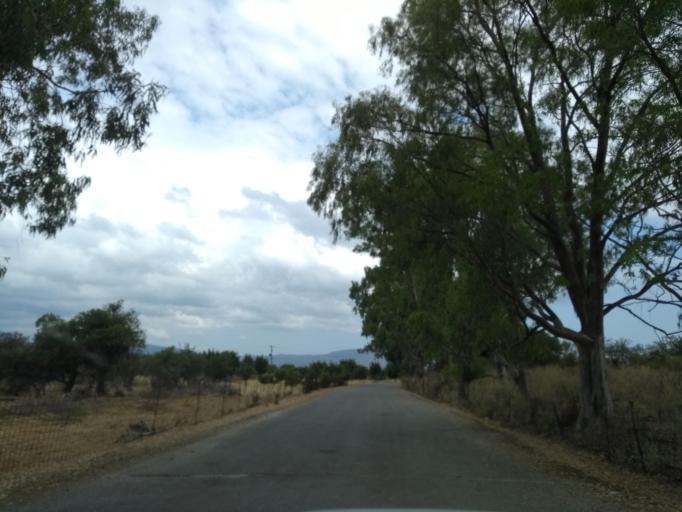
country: GR
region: Crete
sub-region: Nomos Chanias
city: Kalivai
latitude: 35.4062
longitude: 24.2154
